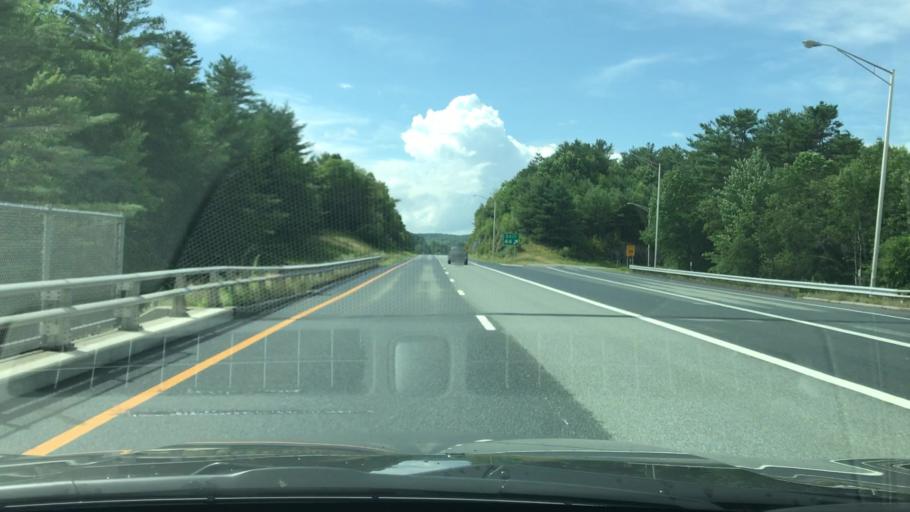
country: US
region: New Hampshire
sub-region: Grafton County
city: Littleton
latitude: 44.3297
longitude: -71.8743
